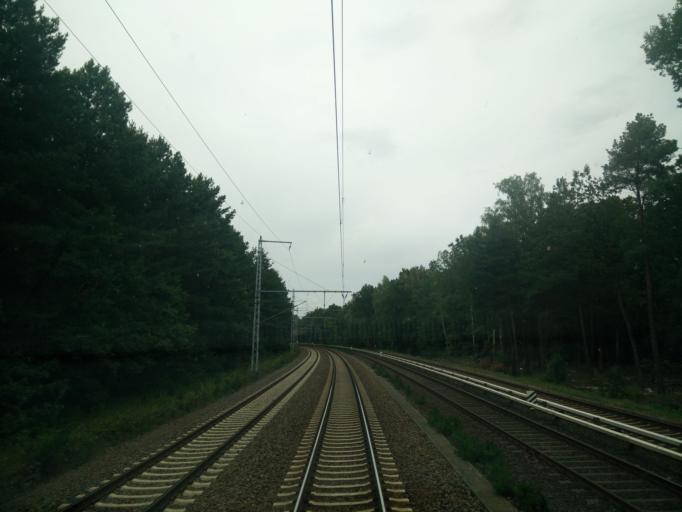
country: DE
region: Berlin
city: Bohnsdorf
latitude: 52.3937
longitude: 13.6006
